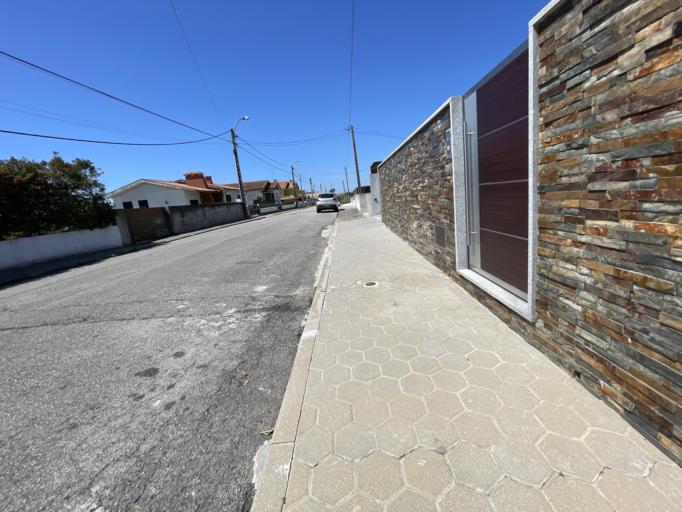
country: PT
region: Aveiro
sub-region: Ovar
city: Cortegaca
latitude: 40.9455
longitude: -8.6266
